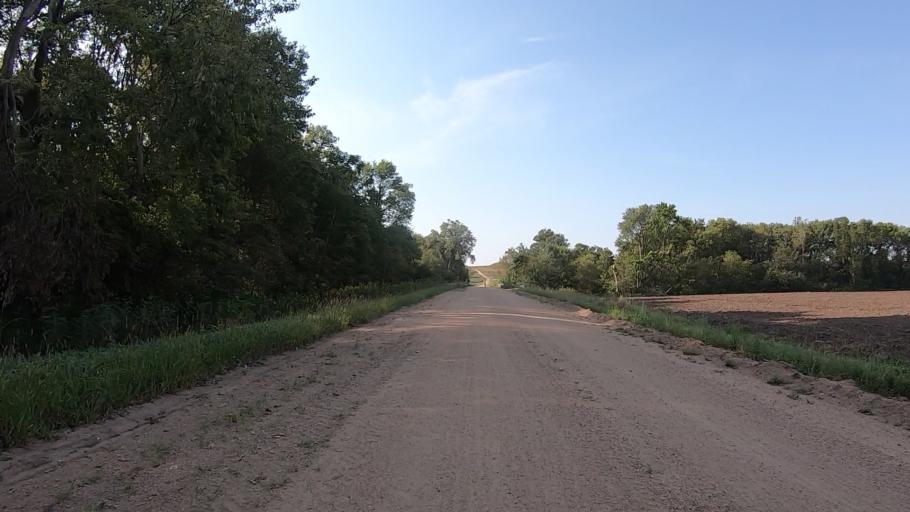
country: US
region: Kansas
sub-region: Marshall County
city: Blue Rapids
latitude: 39.6563
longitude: -96.8815
